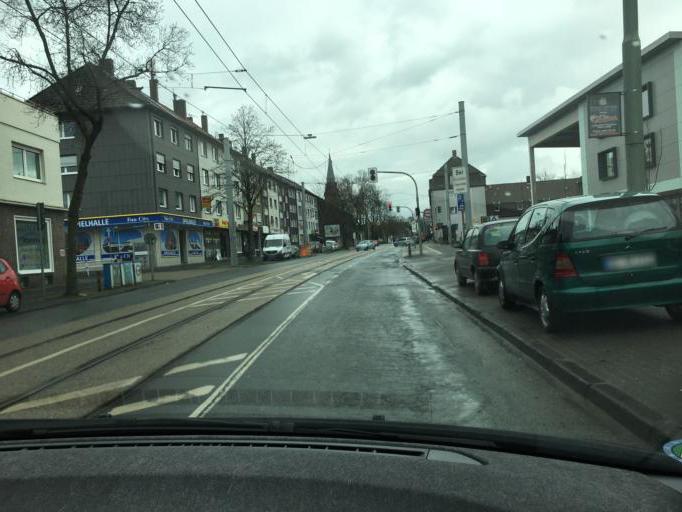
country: DE
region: North Rhine-Westphalia
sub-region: Regierungsbezirk Arnsberg
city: Bochum
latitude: 51.4917
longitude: 7.2437
